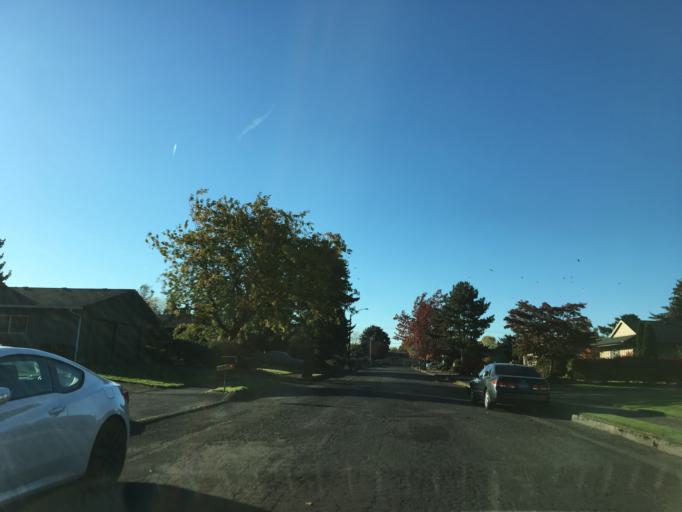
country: US
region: Oregon
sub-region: Multnomah County
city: Gresham
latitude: 45.5066
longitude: -122.4086
